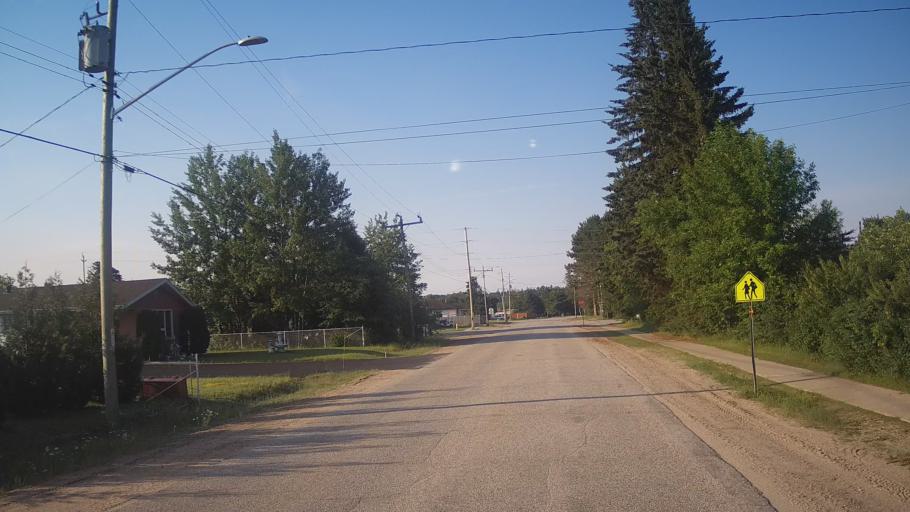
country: CA
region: Ontario
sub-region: Rainy River District
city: Atikokan
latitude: 49.4110
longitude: -91.6574
